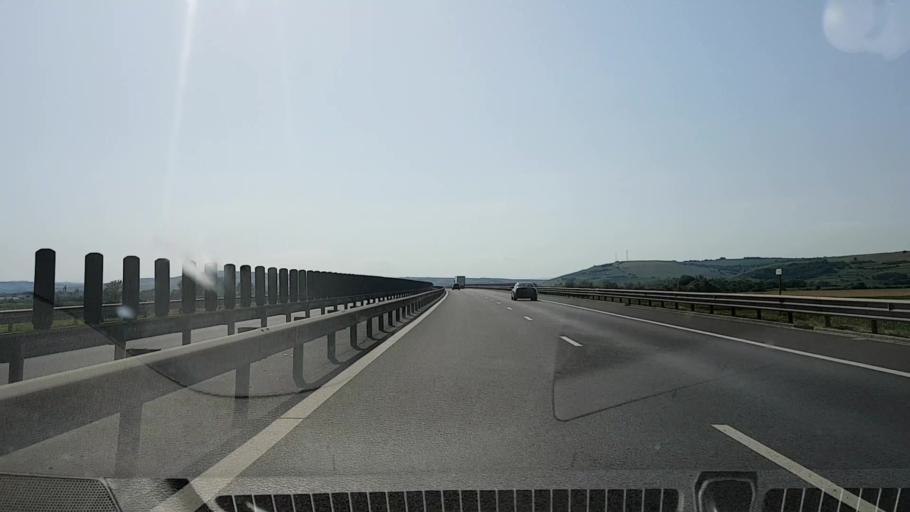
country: RO
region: Sibiu
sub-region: Oras Miercurea Sibiului
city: Miercurea Sibiului
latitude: 45.8964
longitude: 23.8048
